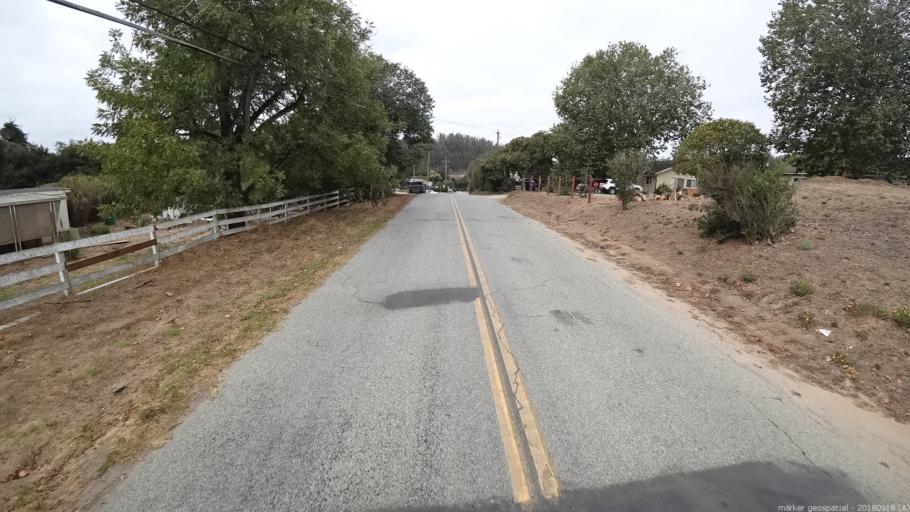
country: US
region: California
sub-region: Monterey County
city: Prunedale
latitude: 36.7877
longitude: -121.6667
